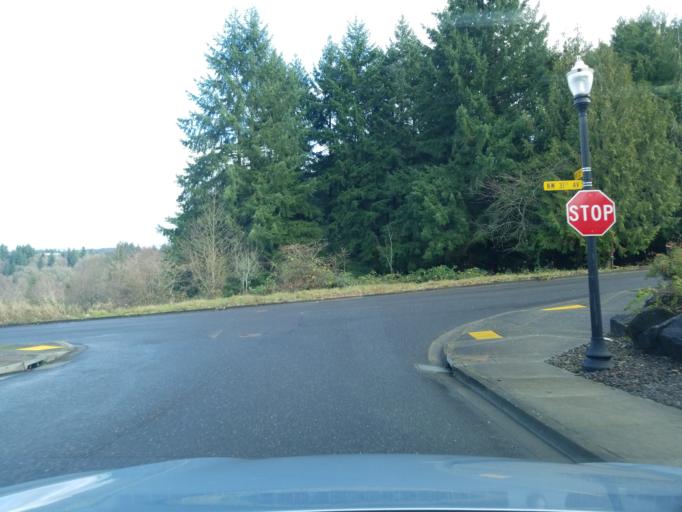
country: US
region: Washington
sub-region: Clark County
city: Felida
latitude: 45.7149
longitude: -122.7032
